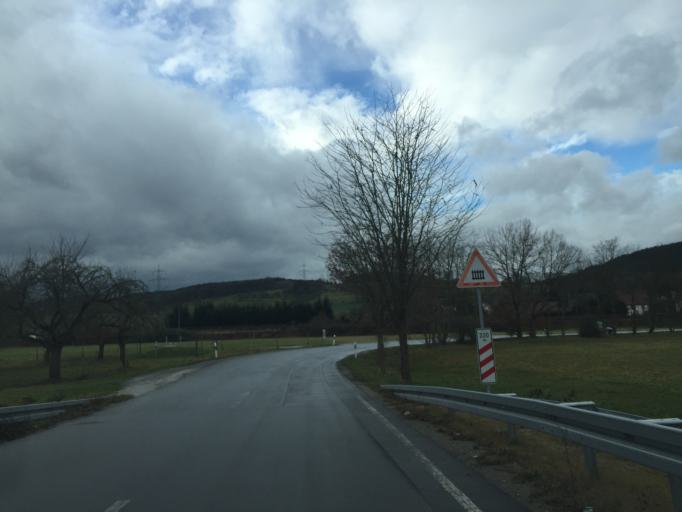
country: DE
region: Thuringia
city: Grosseutersdorf
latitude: 50.7857
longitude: 11.5668
